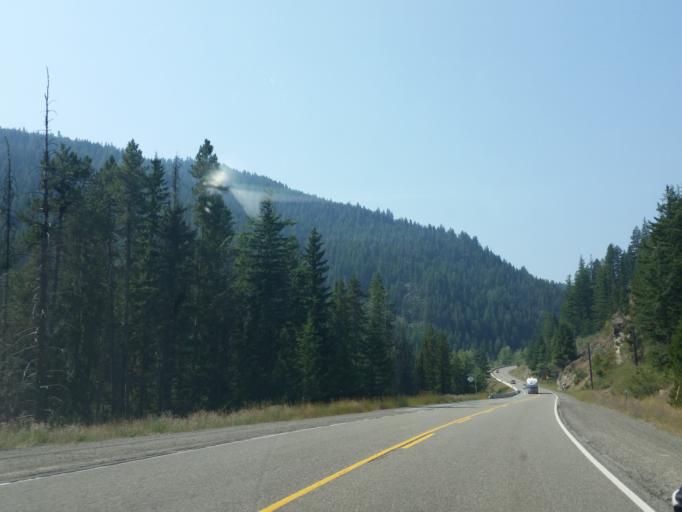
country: CA
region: British Columbia
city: Princeton
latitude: 49.1747
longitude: -120.5525
